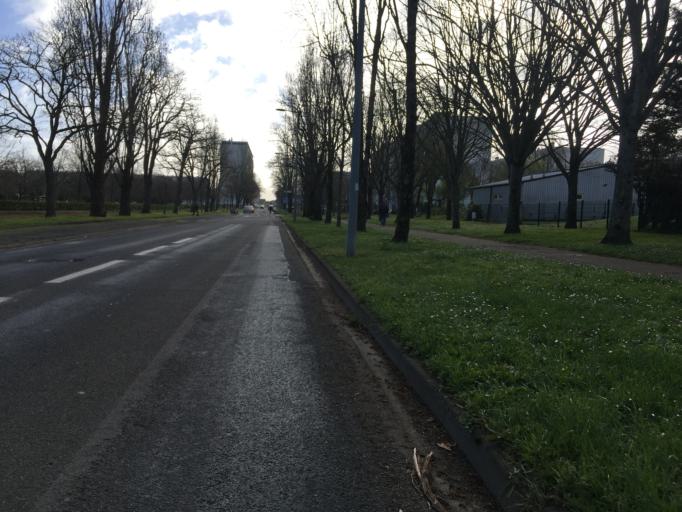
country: FR
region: Poitou-Charentes
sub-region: Departement de la Charente-Maritime
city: La Rochelle
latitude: 46.1679
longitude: -1.1845
